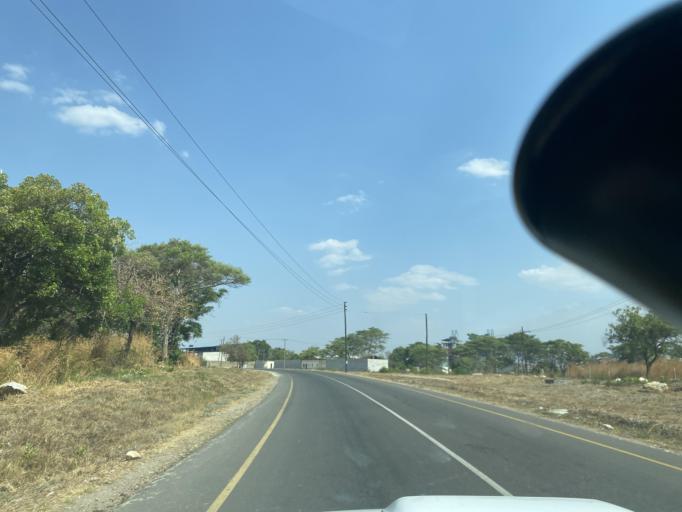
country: ZM
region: Lusaka
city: Lusaka
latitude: -15.3399
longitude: 28.0764
